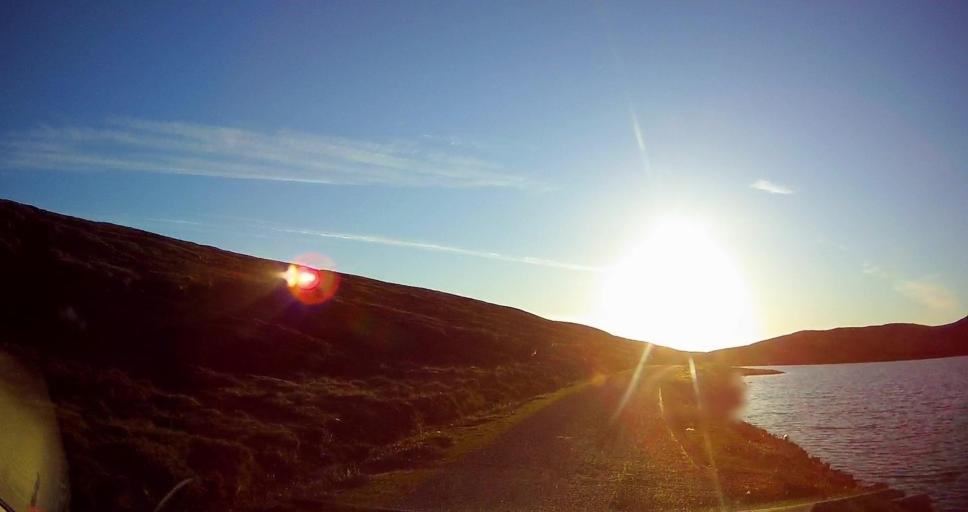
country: GB
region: Scotland
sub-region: Shetland Islands
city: Lerwick
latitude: 60.4430
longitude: -1.4060
